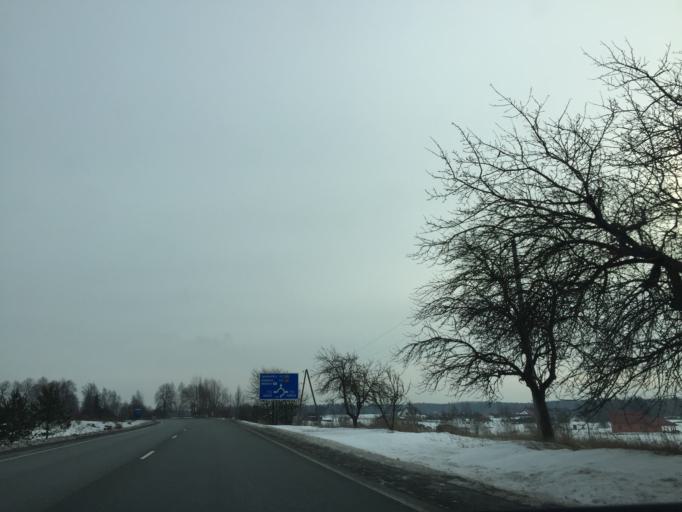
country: LV
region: Ikskile
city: Ikskile
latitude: 56.8674
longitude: 24.5510
